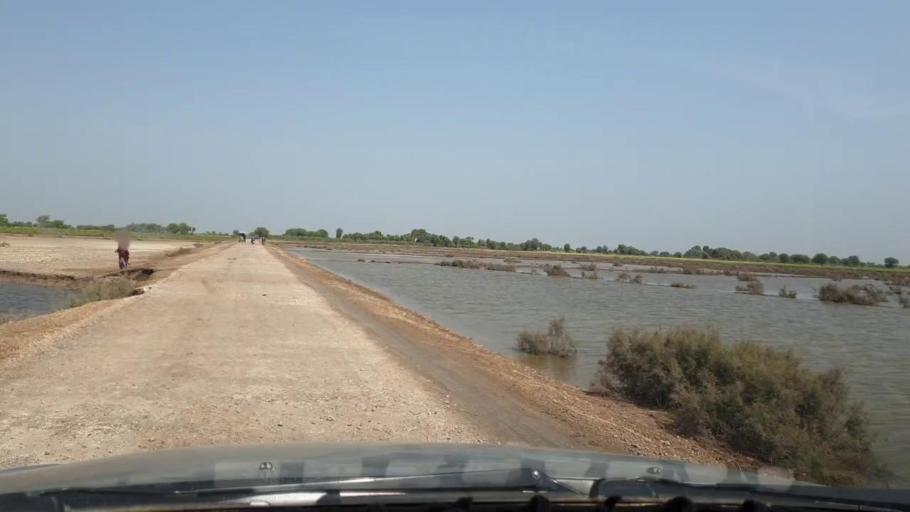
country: PK
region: Sindh
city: Tando Muhammad Khan
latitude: 25.1438
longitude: 68.6328
